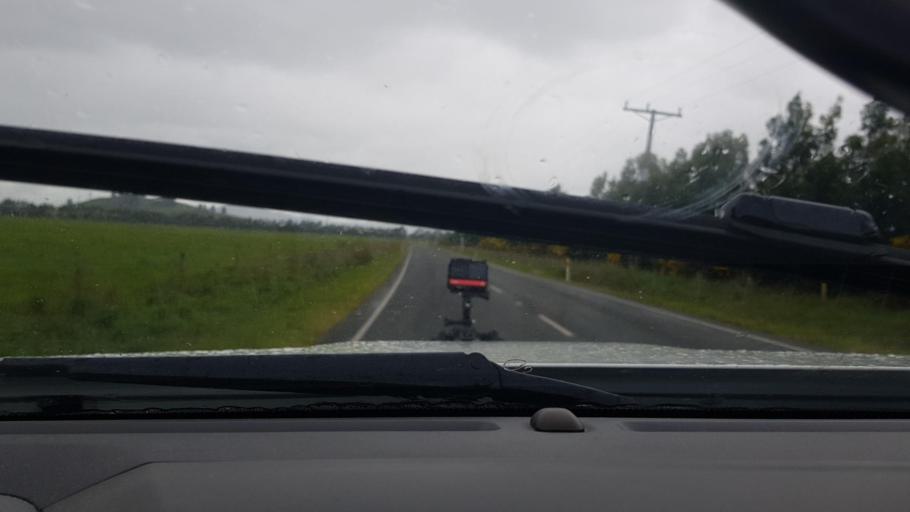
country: NZ
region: Southland
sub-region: Southland District
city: Winton
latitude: -45.7453
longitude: 168.3994
